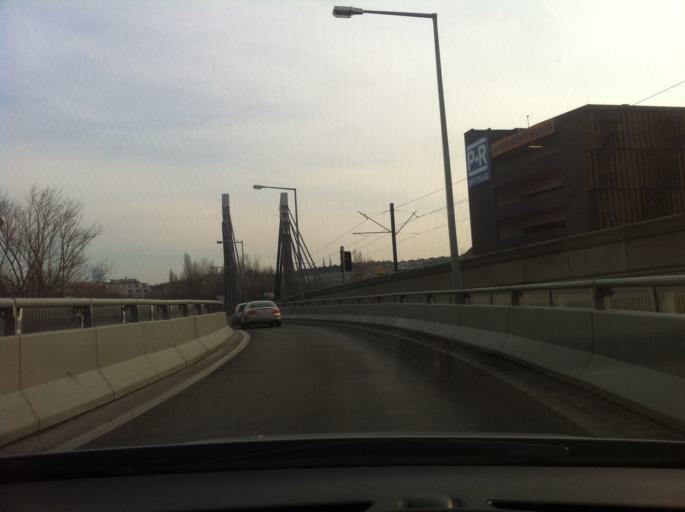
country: AT
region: Vienna
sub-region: Wien Stadt
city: Vienna
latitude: 48.2359
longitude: 16.3604
